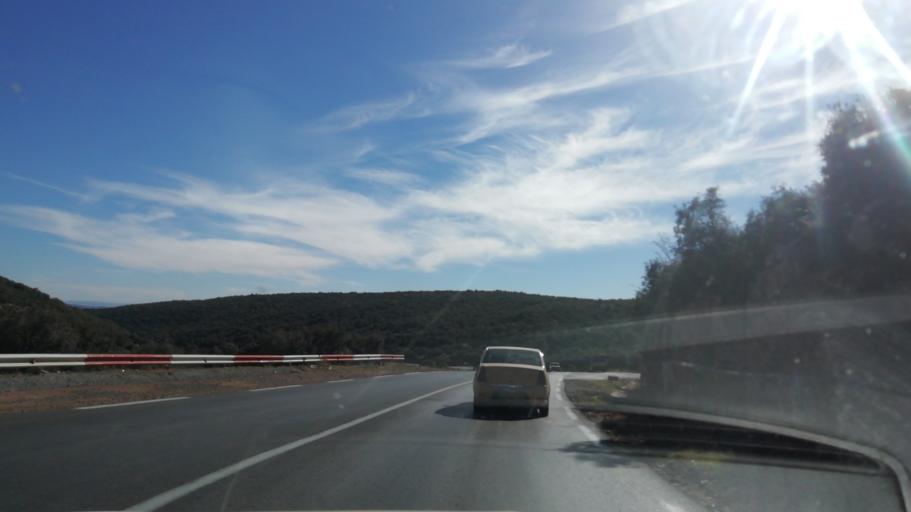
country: DZ
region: Tlemcen
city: Sebdou
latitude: 34.7465
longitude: -1.3497
